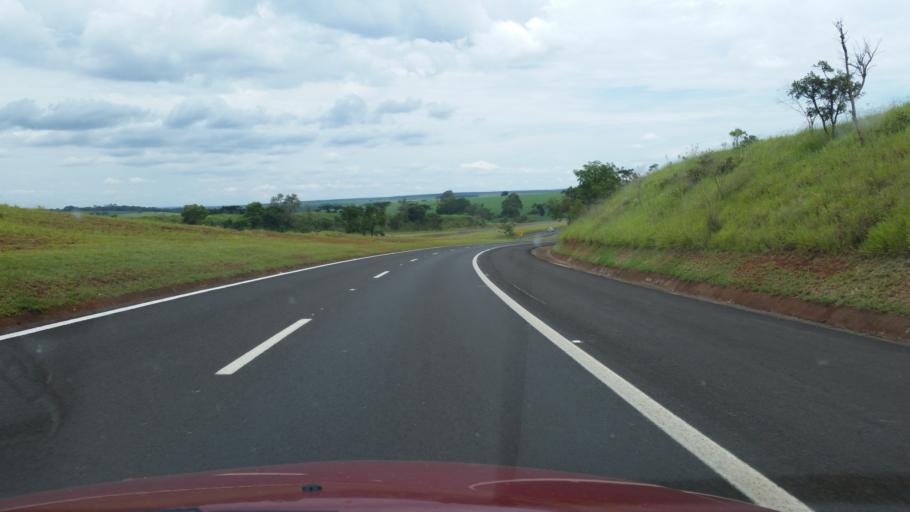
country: BR
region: Sao Paulo
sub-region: Avare
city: Avare
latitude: -22.9663
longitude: -48.8048
